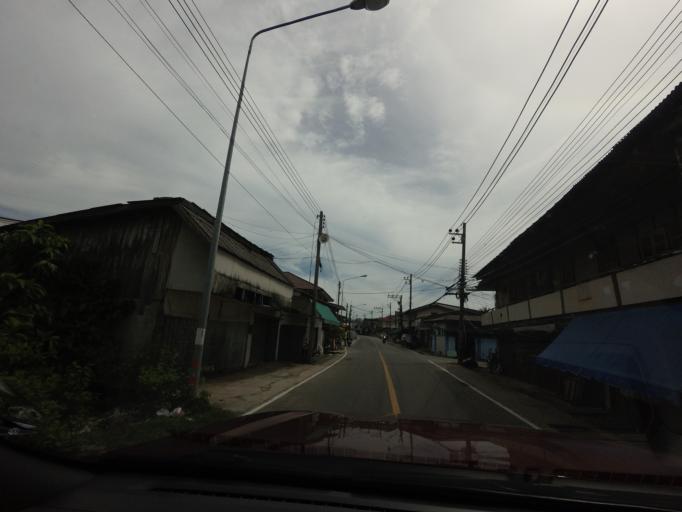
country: TH
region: Narathiwat
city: Tak Bai
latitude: 6.2349
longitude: 102.0879
